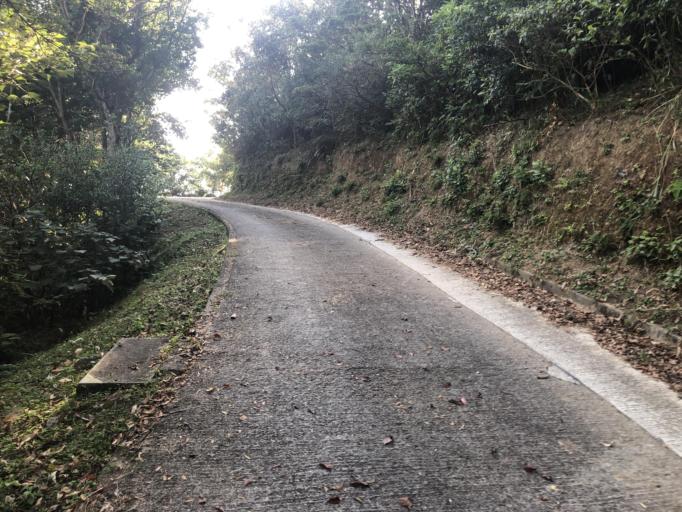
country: HK
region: Tsuen Wan
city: Tsuen Wan
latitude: 22.3987
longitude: 114.0913
